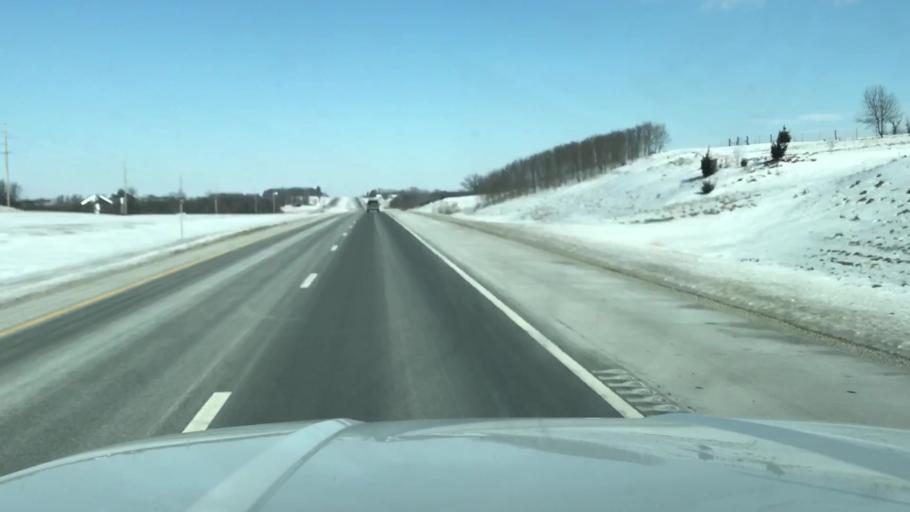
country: US
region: Missouri
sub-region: Nodaway County
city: Maryville
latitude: 40.1912
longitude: -94.8678
